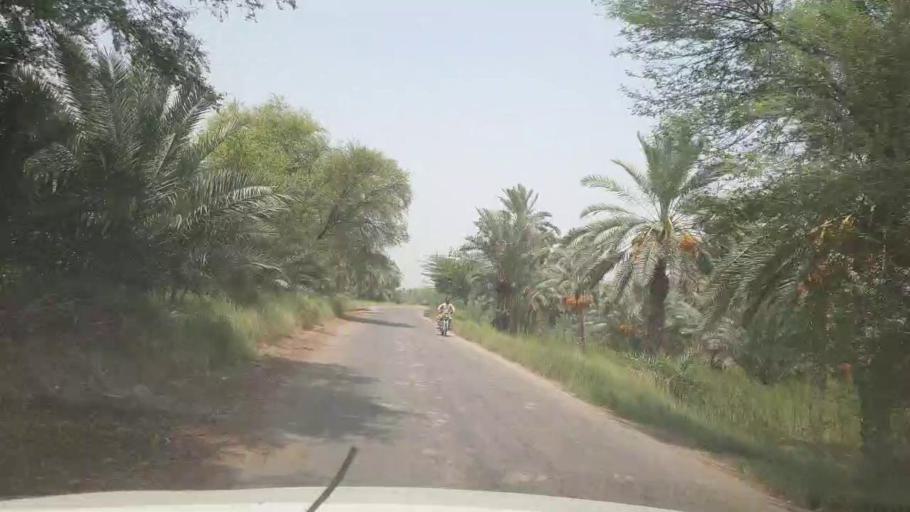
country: PK
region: Sindh
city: Kot Diji
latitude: 27.3625
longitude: 68.6874
